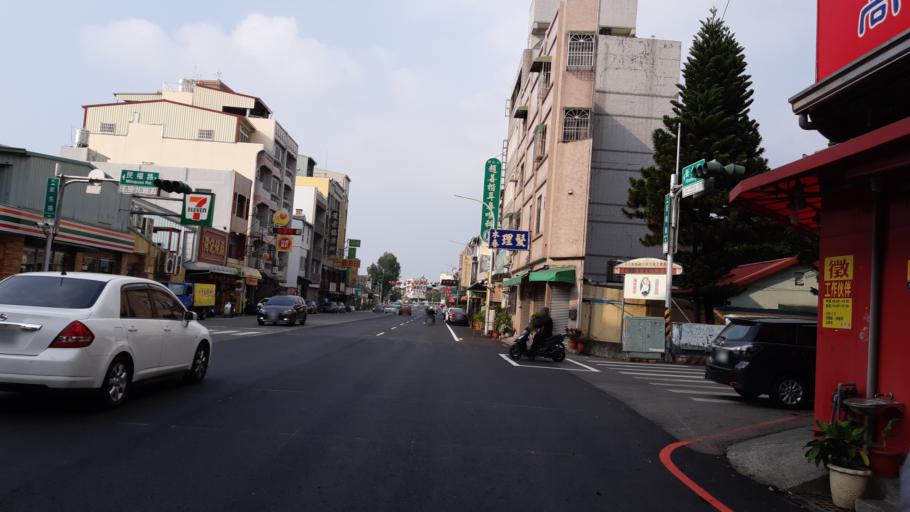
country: TW
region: Taiwan
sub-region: Chiayi
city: Jiayi Shi
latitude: 23.4840
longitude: 120.4610
